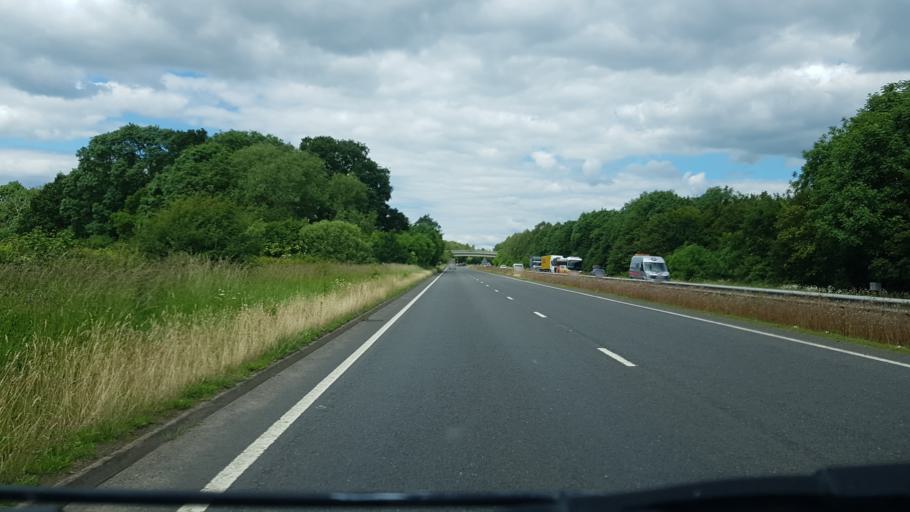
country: GB
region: England
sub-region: Warwickshire
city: Alcester
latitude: 52.2136
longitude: -1.8827
